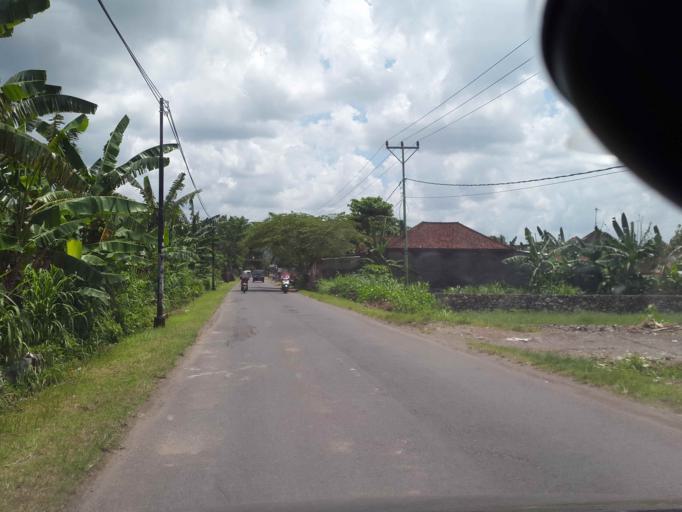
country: ID
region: West Nusa Tenggara
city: Mambalan
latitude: -8.5405
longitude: 116.0809
